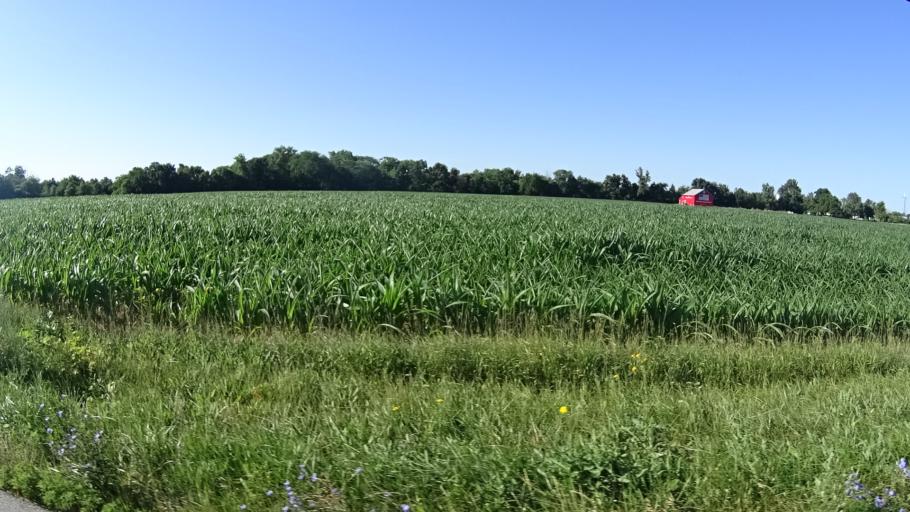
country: US
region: Ohio
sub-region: Erie County
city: Sandusky
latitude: 41.3978
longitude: -82.7674
